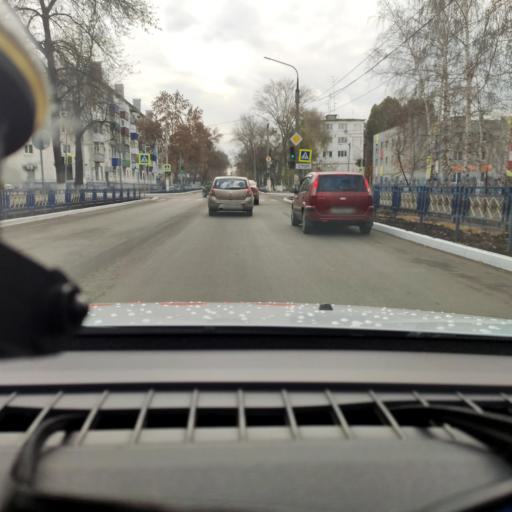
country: RU
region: Samara
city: Chapayevsk
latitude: 52.9844
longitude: 49.7197
